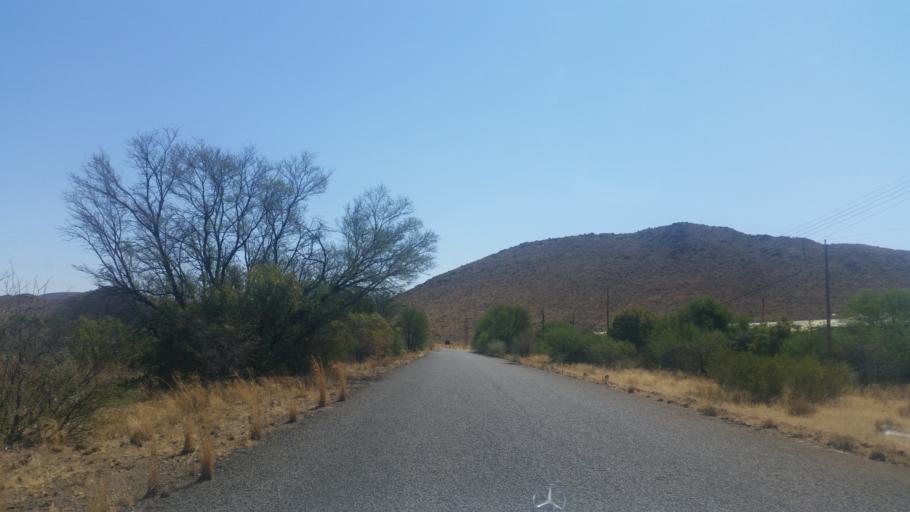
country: ZA
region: Northern Cape
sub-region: Pixley ka Seme District Municipality
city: Colesberg
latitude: -30.6244
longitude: 25.4801
